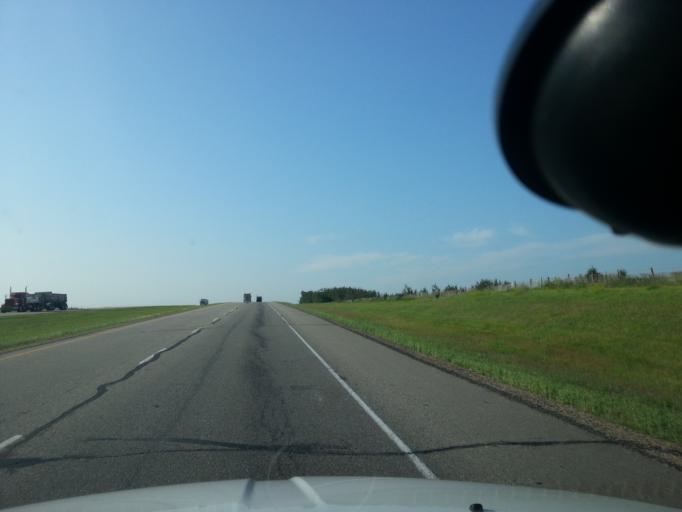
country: CA
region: Alberta
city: Millet
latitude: 53.0599
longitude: -113.5984
